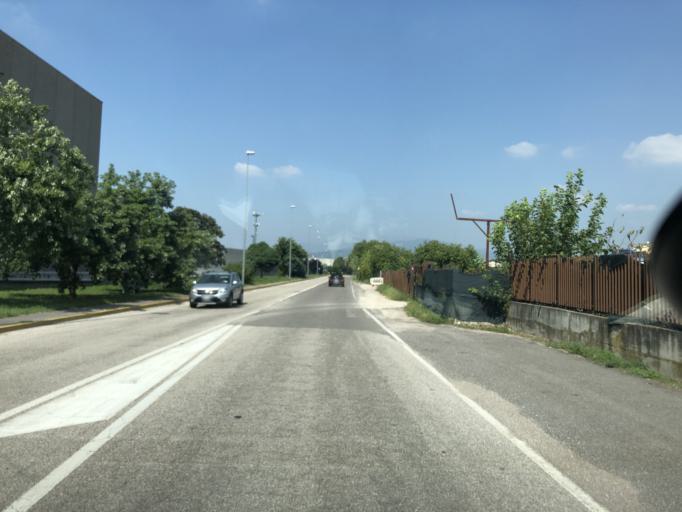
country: IT
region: Veneto
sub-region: Provincia di Verona
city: Bassone
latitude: 45.4486
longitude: 10.8972
